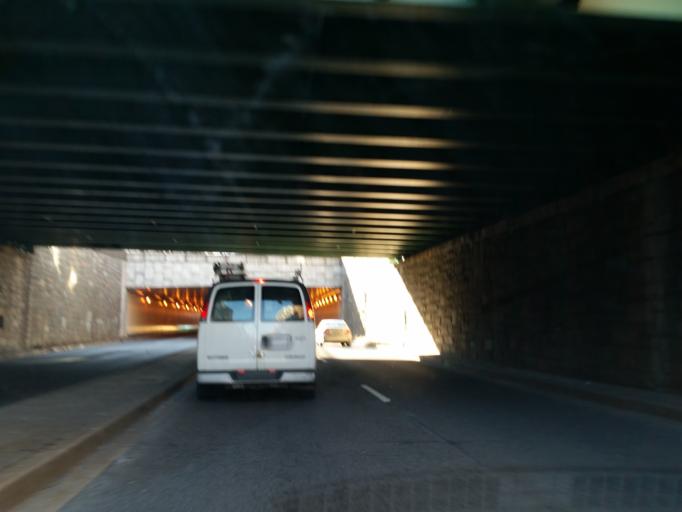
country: US
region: Washington, D.C.
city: Washington, D.C.
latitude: 38.9025
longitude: -77.0484
